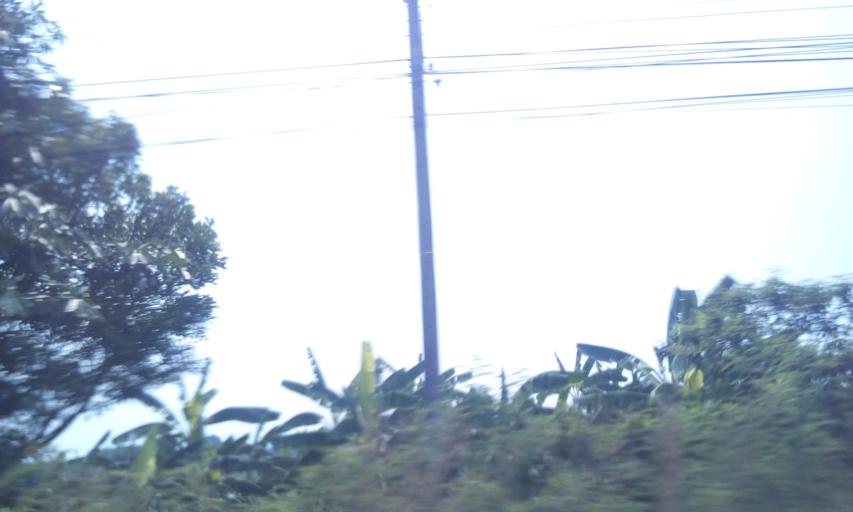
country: TH
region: Nonthaburi
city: Sai Noi
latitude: 13.9344
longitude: 100.3171
